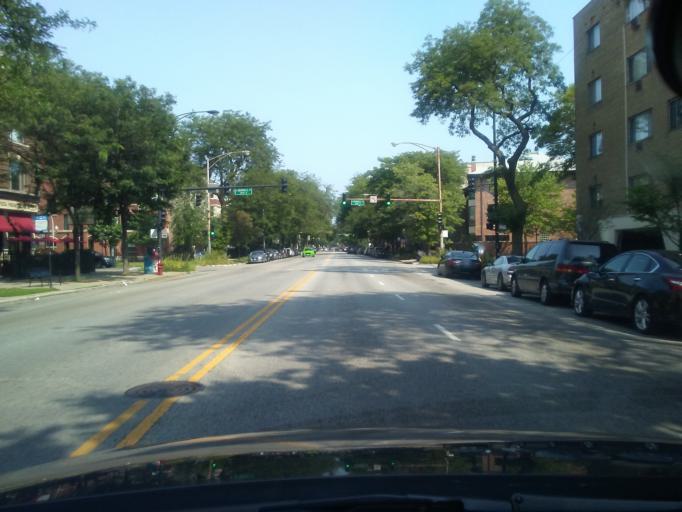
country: US
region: Illinois
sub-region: Cook County
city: Evanston
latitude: 42.0064
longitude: -87.6611
